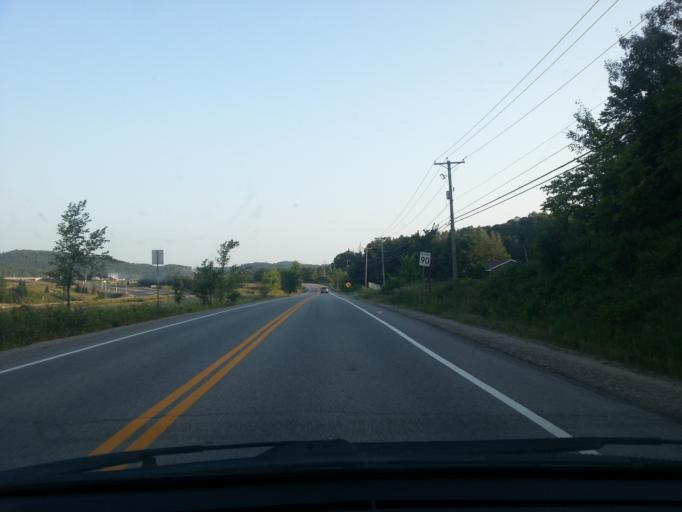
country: CA
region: Quebec
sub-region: Outaouais
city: Wakefield
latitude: 45.5909
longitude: -75.8908
